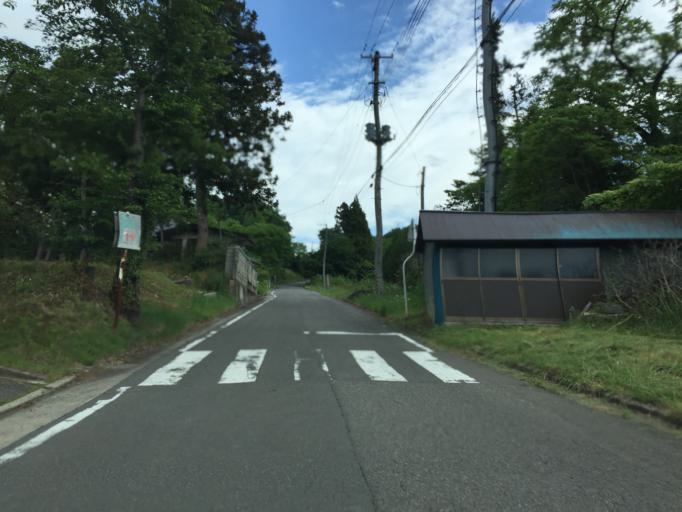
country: JP
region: Fukushima
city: Nihommatsu
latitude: 37.6376
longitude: 140.5015
